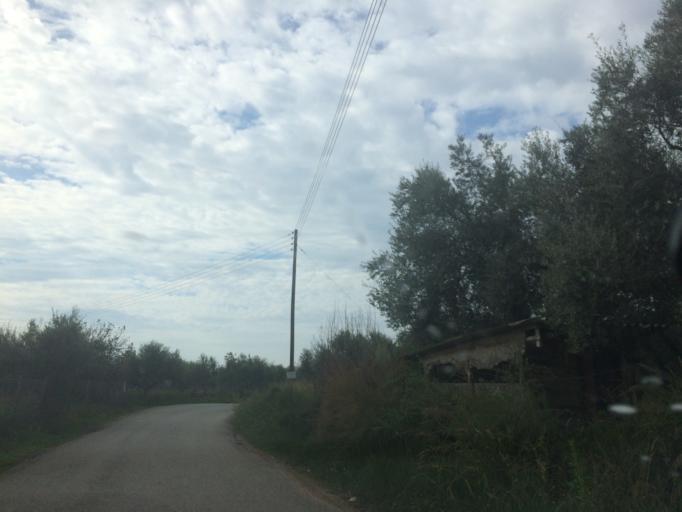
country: GR
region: Peloponnese
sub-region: Nomos Messinias
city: Khora
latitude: 36.9885
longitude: 21.6694
